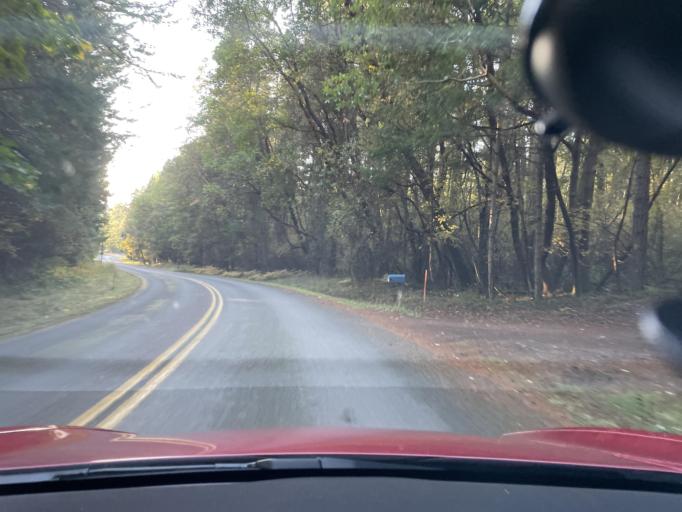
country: US
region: Washington
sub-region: San Juan County
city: Friday Harbor
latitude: 48.5506
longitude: -123.1598
